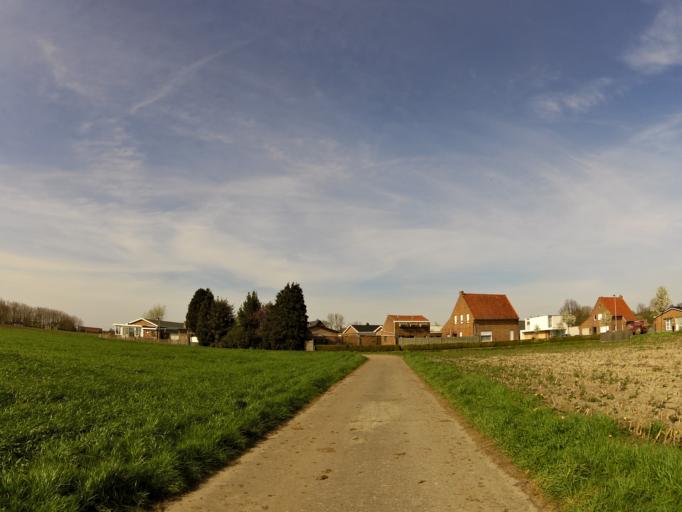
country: BE
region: Flanders
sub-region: Provincie West-Vlaanderen
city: Oudenburg
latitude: 51.1539
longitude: 3.0216
